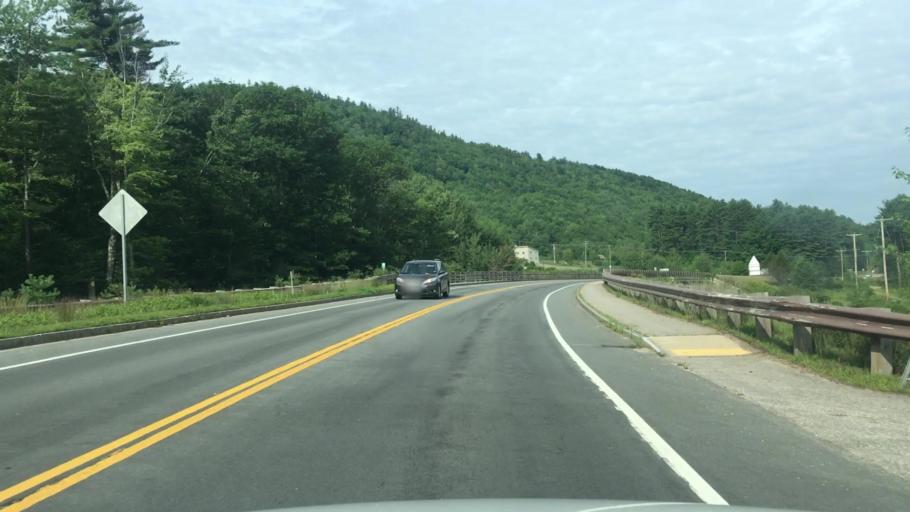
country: US
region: New Hampshire
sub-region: Carroll County
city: Tamworth
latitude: 43.8192
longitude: -71.2050
